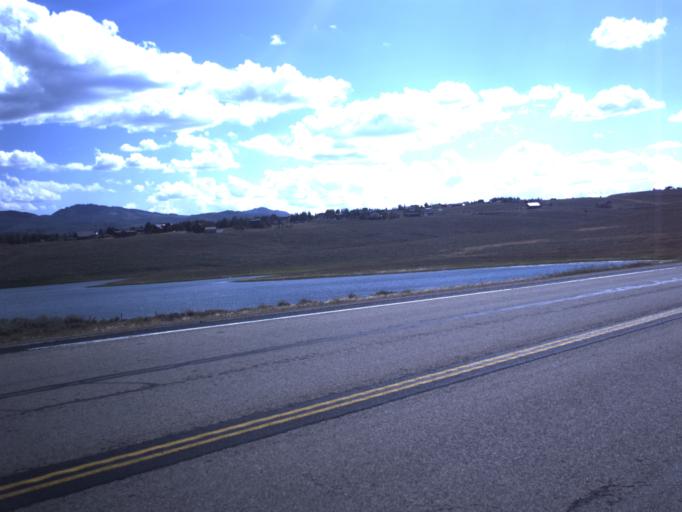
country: US
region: Utah
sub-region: Summit County
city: Francis
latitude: 40.1822
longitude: -111.0306
